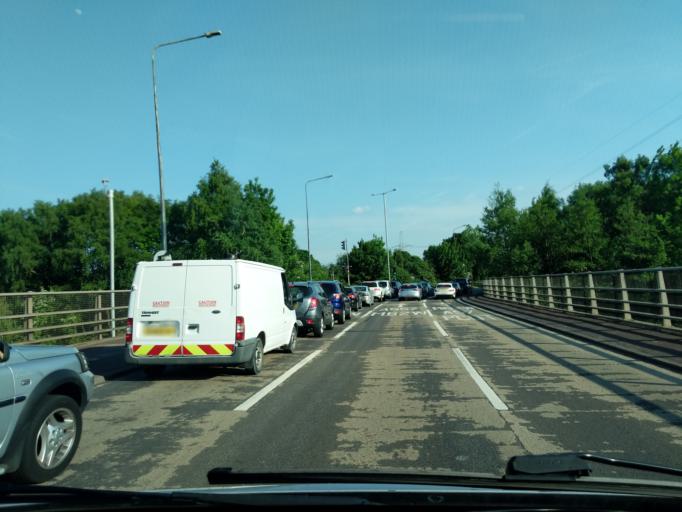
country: GB
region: England
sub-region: Borough of Halton
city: Widnes
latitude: 53.4039
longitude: -2.7442
